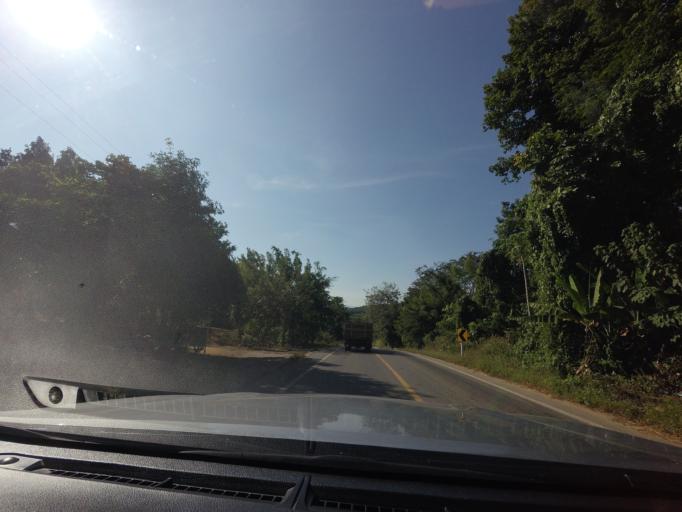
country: TH
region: Phrae
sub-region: Amphoe Wang Chin
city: Wang Chin
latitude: 17.7081
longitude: 99.6910
